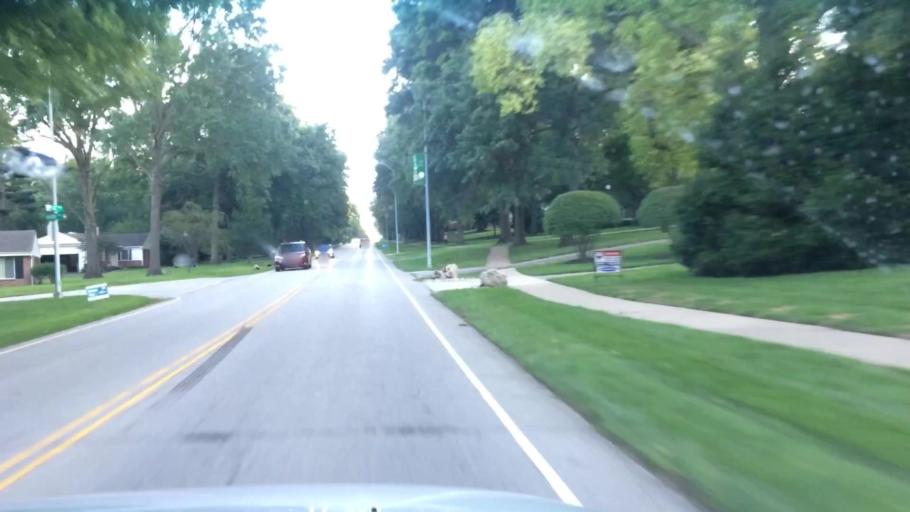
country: US
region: Kansas
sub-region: Johnson County
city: Leawood
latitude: 38.9732
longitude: -94.6145
